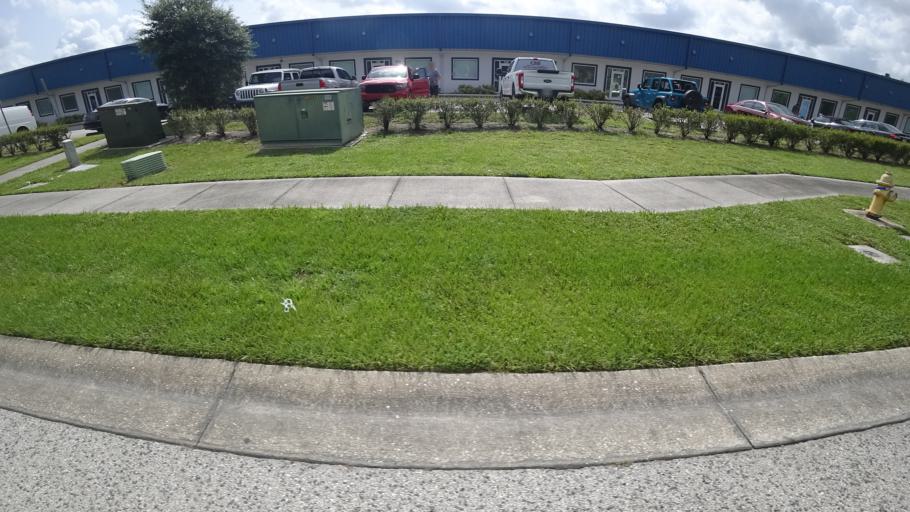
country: US
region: Florida
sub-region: Sarasota County
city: Desoto Lakes
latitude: 27.4500
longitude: -82.4560
